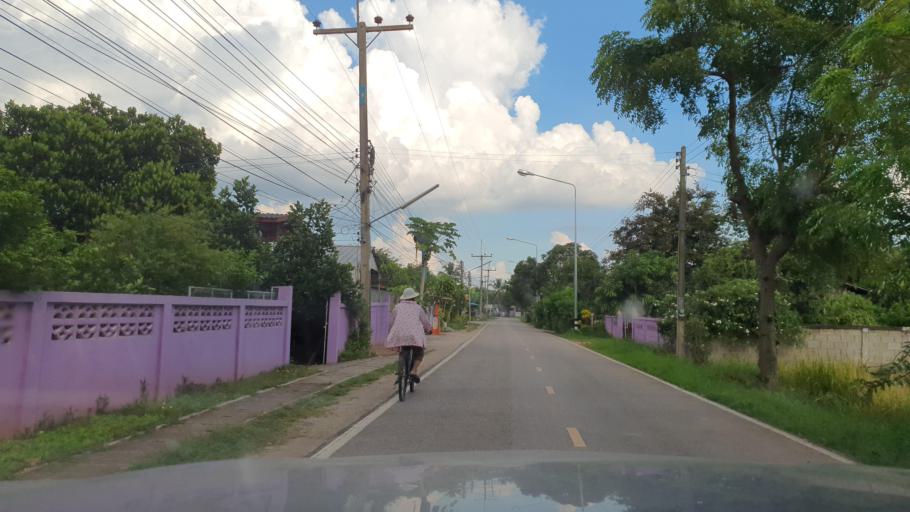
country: TH
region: Phayao
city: Phayao
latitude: 19.1799
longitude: 99.8400
